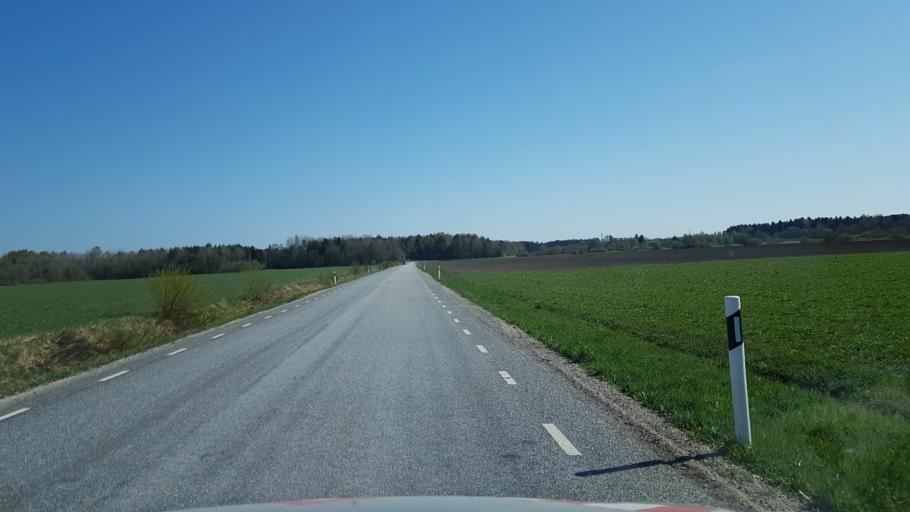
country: EE
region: Harju
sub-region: Saue linn
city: Saue
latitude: 59.3354
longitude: 24.5687
